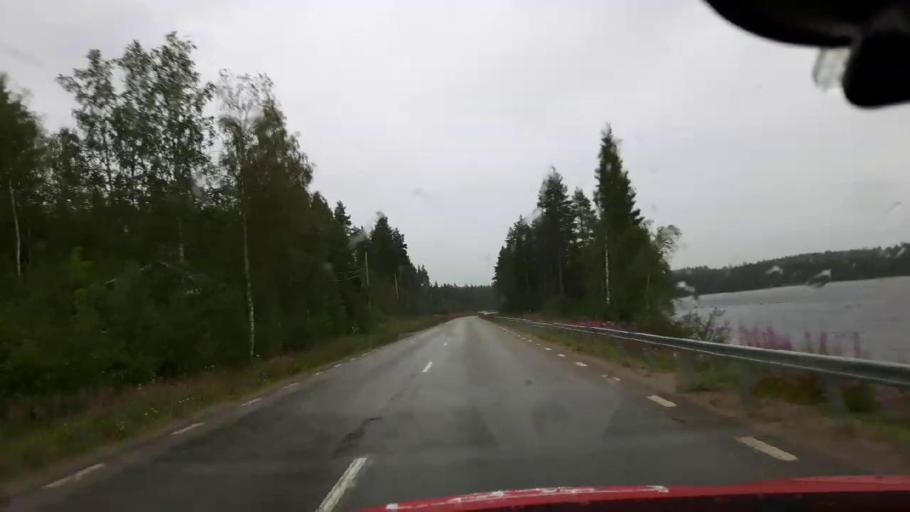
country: SE
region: Jaemtland
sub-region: OEstersunds Kommun
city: Brunflo
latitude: 62.7821
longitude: 15.0112
